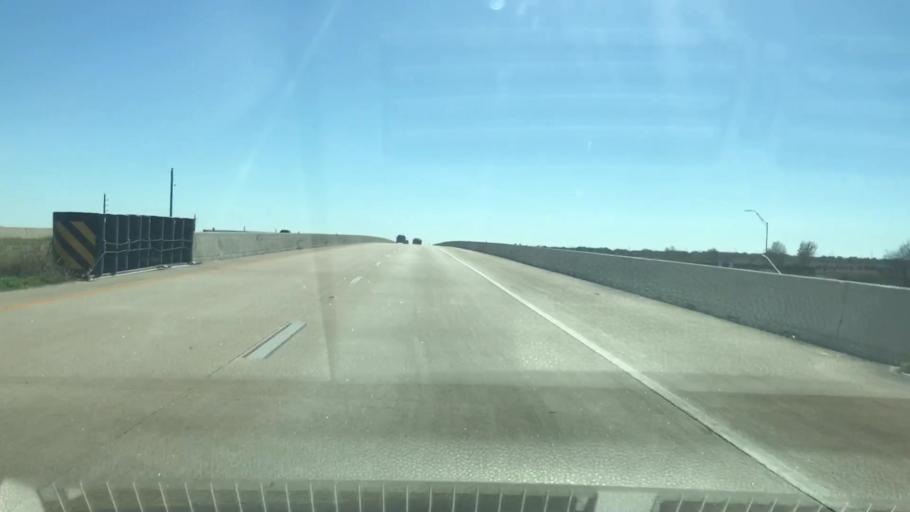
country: US
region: Texas
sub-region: Harris County
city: Cypress
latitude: 29.9799
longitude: -95.7697
